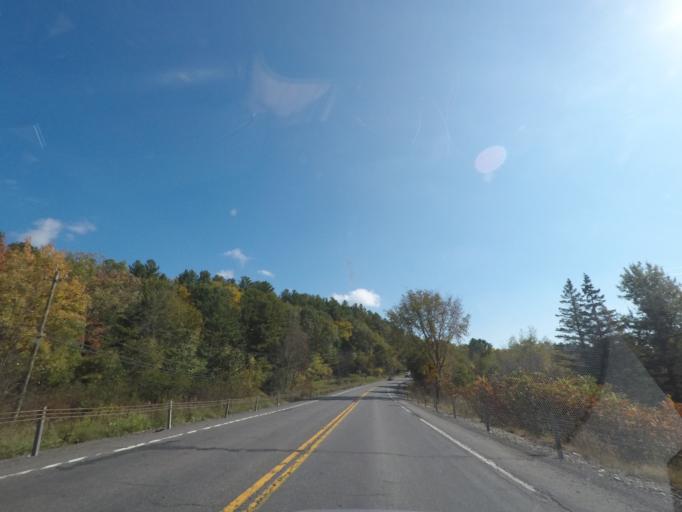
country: US
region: New York
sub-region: Rensselaer County
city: Averill Park
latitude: 42.6401
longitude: -73.5689
